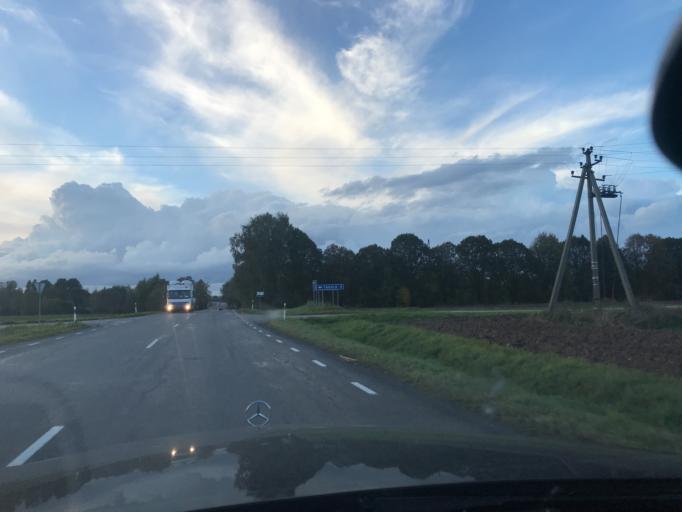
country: EE
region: Vorumaa
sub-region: Antsla vald
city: Vana-Antsla
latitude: 57.8905
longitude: 26.5054
